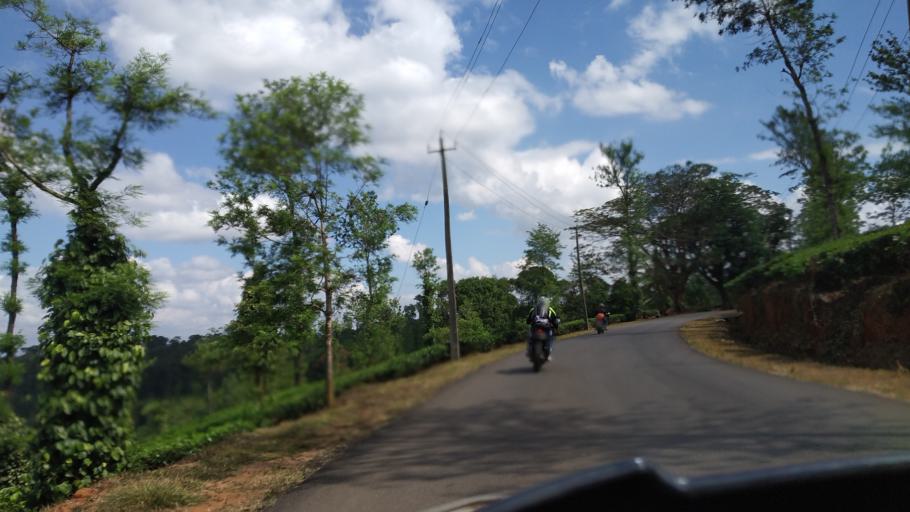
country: IN
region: Karnataka
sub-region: Kodagu
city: Ponnampet
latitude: 12.0318
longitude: 75.9412
